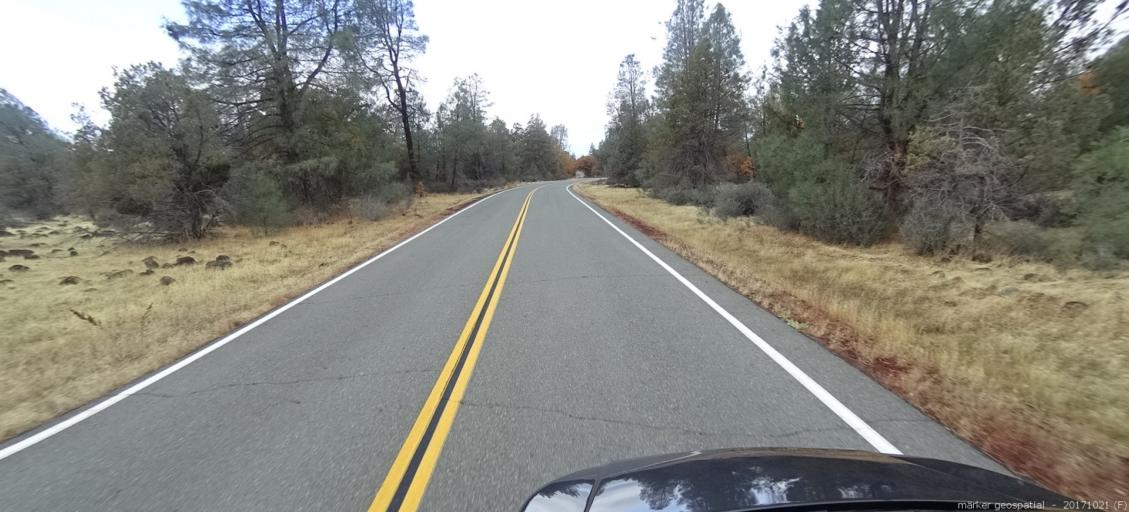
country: US
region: California
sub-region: Shasta County
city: Burney
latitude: 40.9224
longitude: -121.5181
